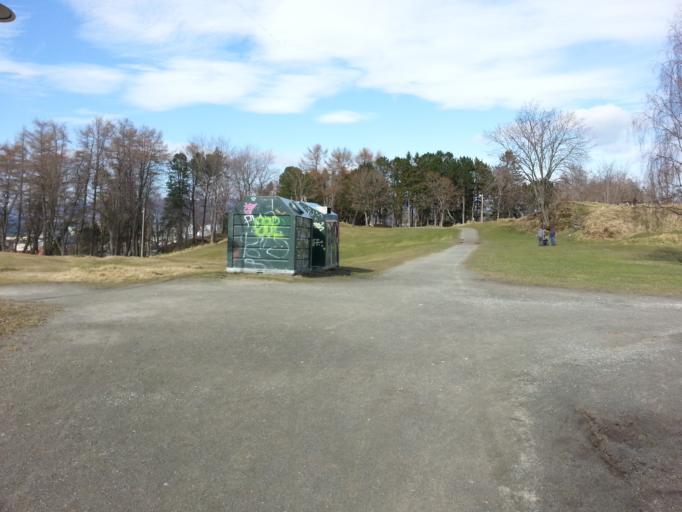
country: NO
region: Sor-Trondelag
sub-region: Trondheim
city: Trondheim
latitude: 63.4279
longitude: 10.4116
